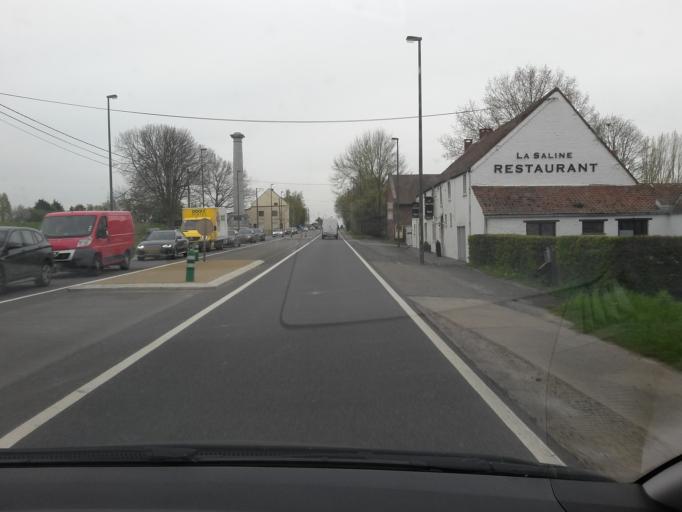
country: BE
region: Wallonia
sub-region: Province du Brabant Wallon
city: Braine-l'Alleud
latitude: 50.6677
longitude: 4.4133
